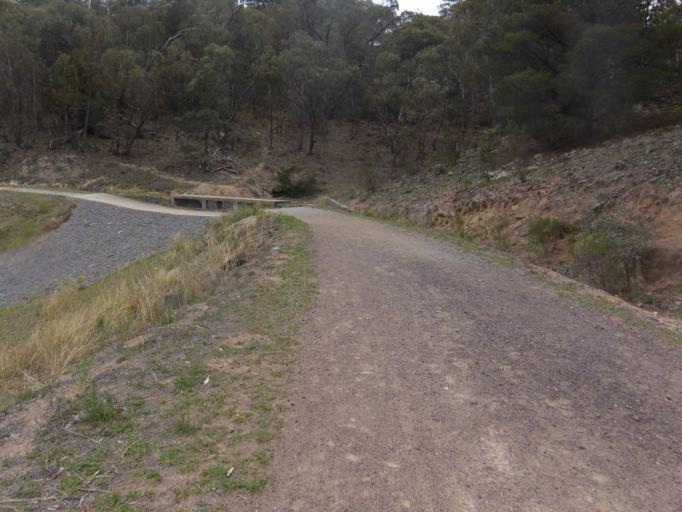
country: AU
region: Australian Capital Territory
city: Forrest
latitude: -35.3610
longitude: 149.1136
